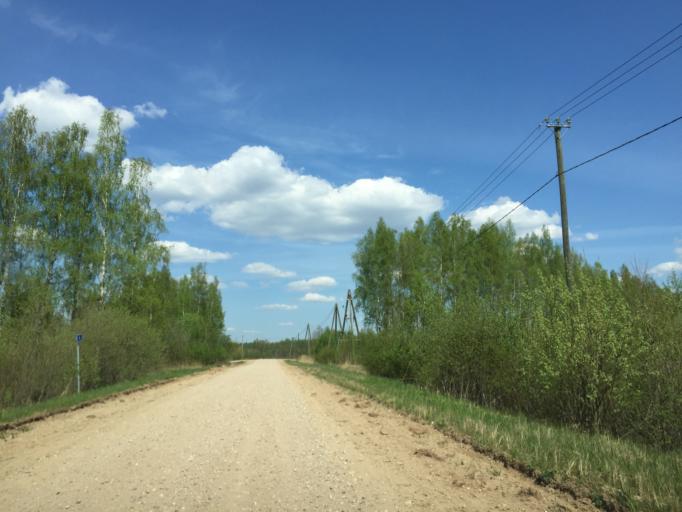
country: LV
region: Limbazu Rajons
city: Limbazi
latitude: 57.3921
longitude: 24.5725
